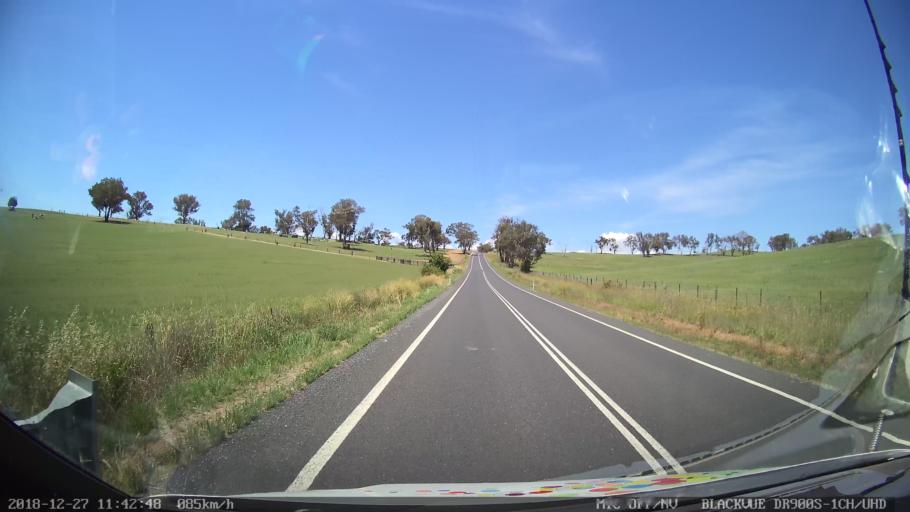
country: AU
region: New South Wales
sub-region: Bathurst Regional
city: Perthville
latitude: -33.5528
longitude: 149.4773
